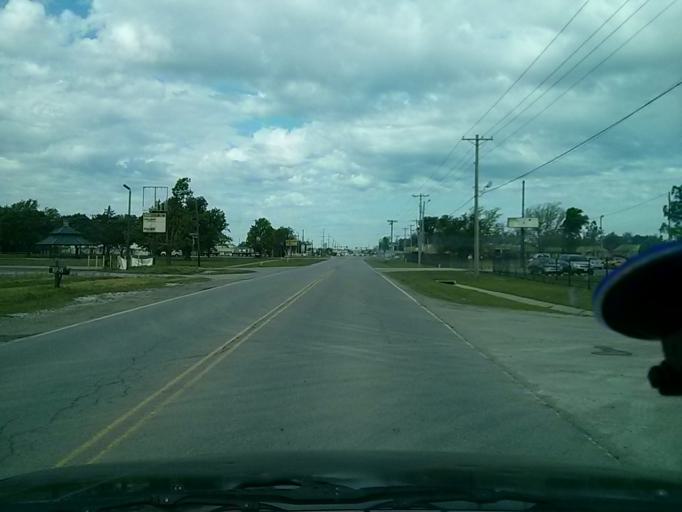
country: US
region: Oklahoma
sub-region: Rogers County
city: Catoosa
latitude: 36.1607
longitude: -95.8459
